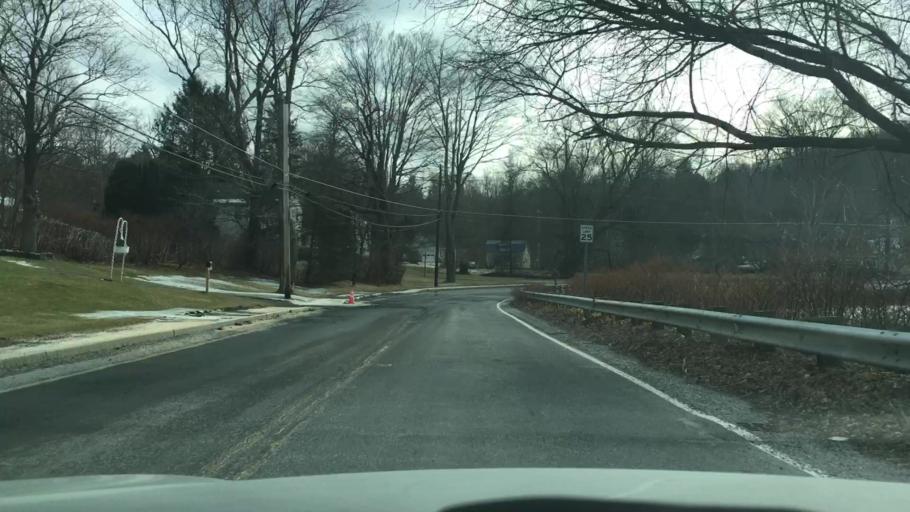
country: US
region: Massachusetts
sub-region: Berkshire County
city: Lee
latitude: 42.3132
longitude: -73.2458
